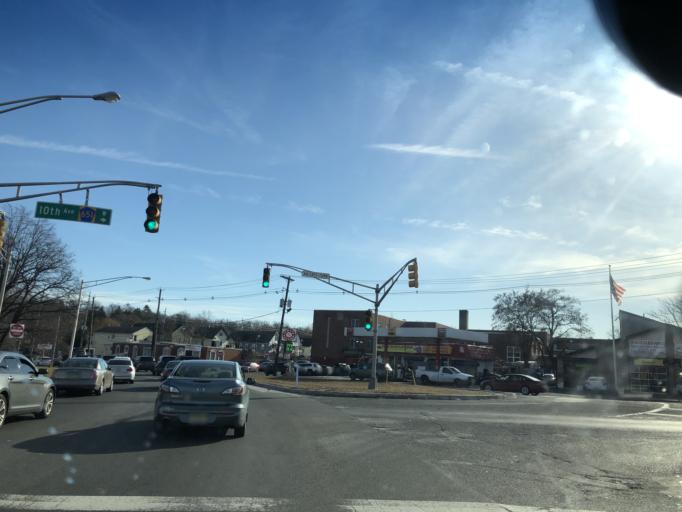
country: US
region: New Jersey
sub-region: Bergen County
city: Fair Lawn
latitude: 40.9235
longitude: -74.1423
